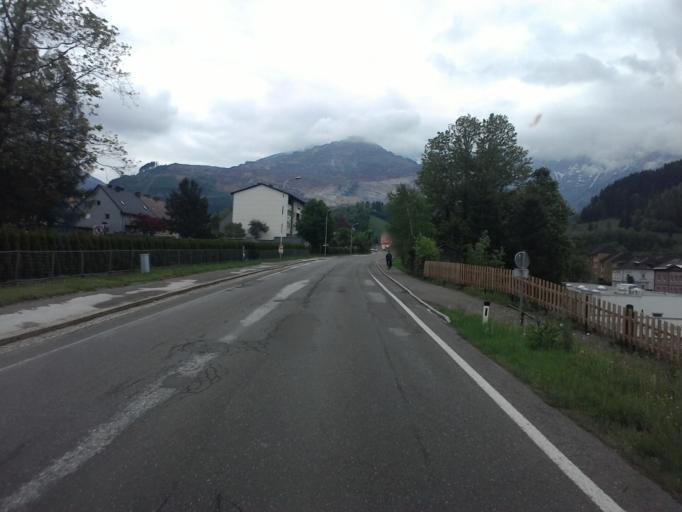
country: AT
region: Styria
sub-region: Politischer Bezirk Leoben
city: Eisenerz
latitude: 47.5468
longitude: 14.8813
